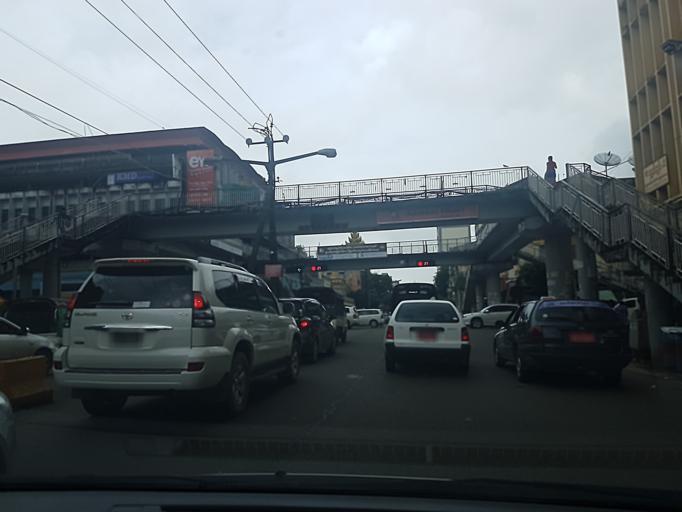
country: MM
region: Yangon
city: Yangon
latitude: 16.7747
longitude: 96.1527
